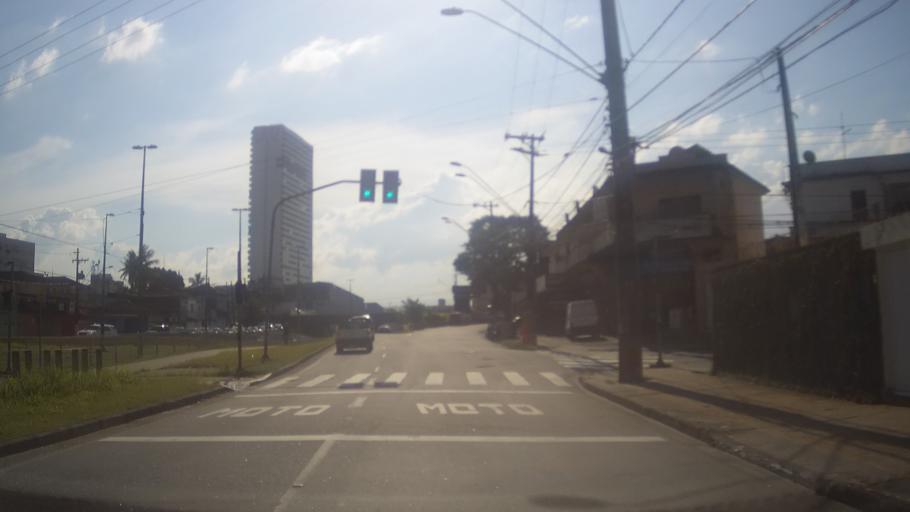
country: BR
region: Sao Paulo
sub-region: Sao Vicente
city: Sao Vicente
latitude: -23.9645
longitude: -46.3808
